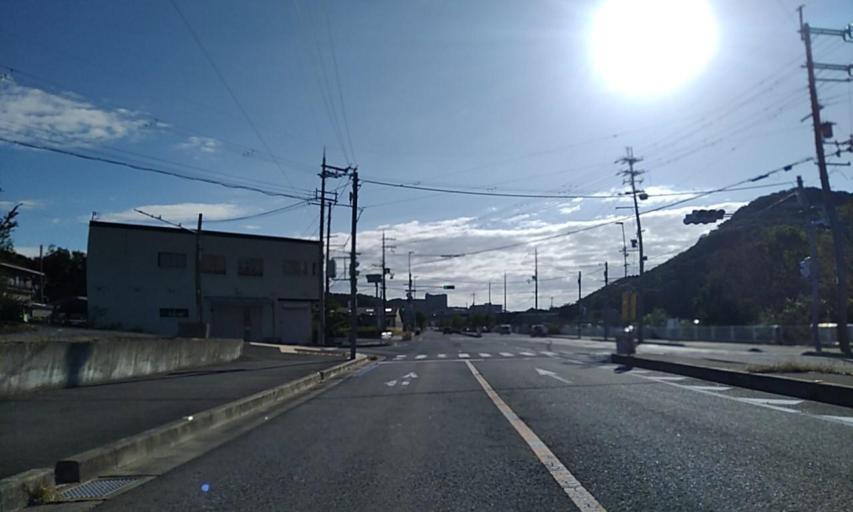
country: JP
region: Wakayama
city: Minato
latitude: 34.2690
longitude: 135.0891
